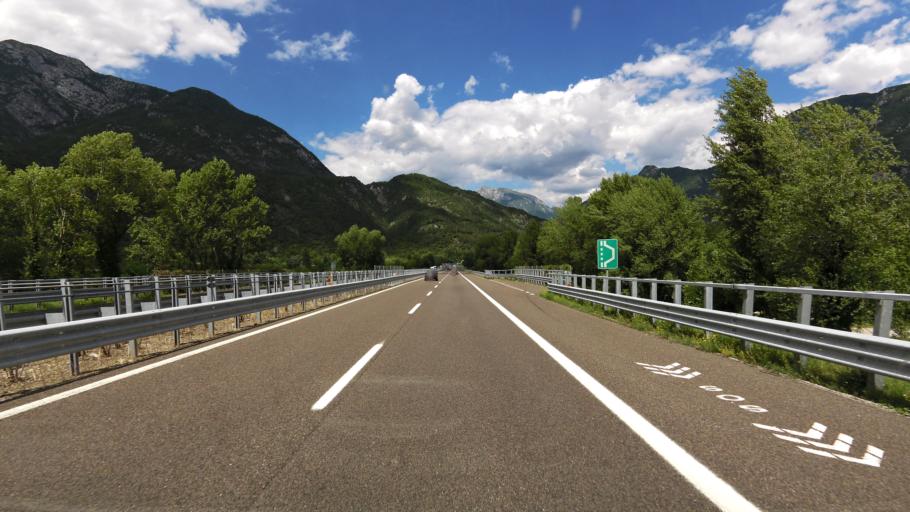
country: IT
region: Friuli Venezia Giulia
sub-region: Provincia di Udine
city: Trasaghis
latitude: 46.3158
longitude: 13.0601
